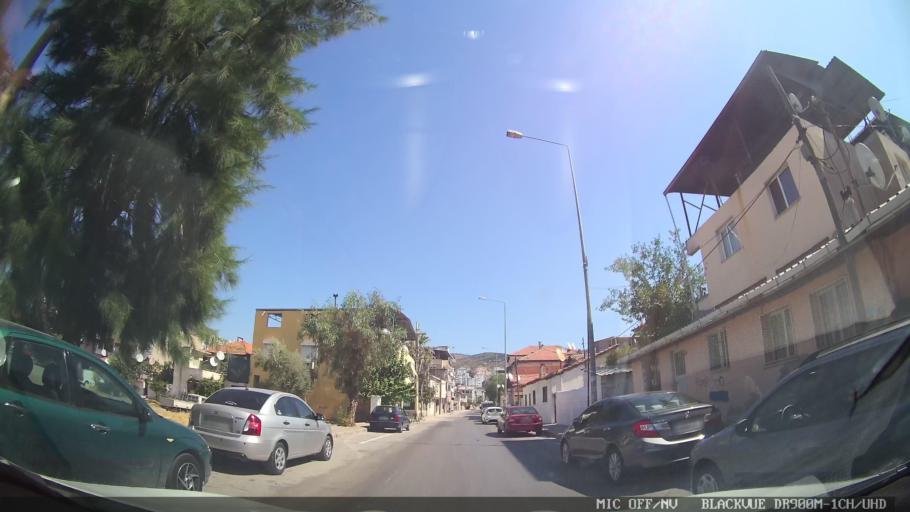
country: TR
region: Izmir
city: Karsiyaka
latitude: 38.4945
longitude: 27.0658
